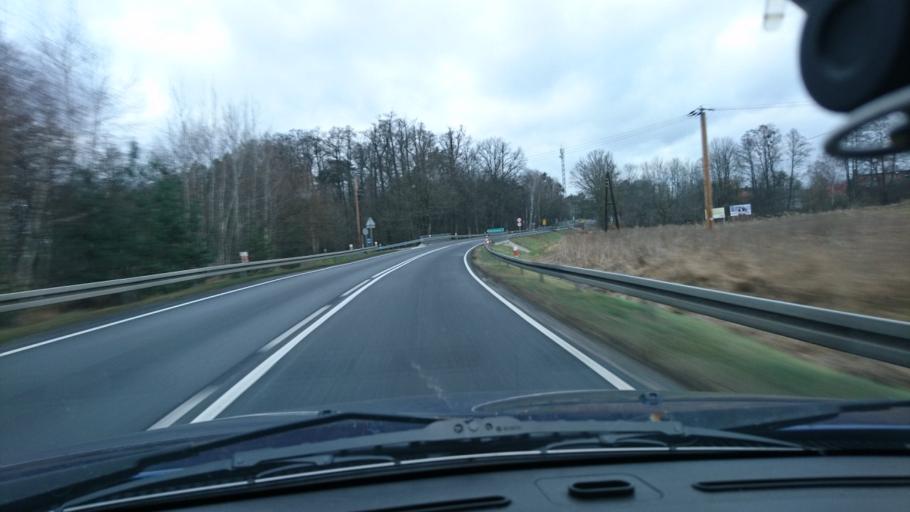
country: PL
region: Opole Voivodeship
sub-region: Powiat kluczborski
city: Kluczbork
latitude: 50.9541
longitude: 18.3091
